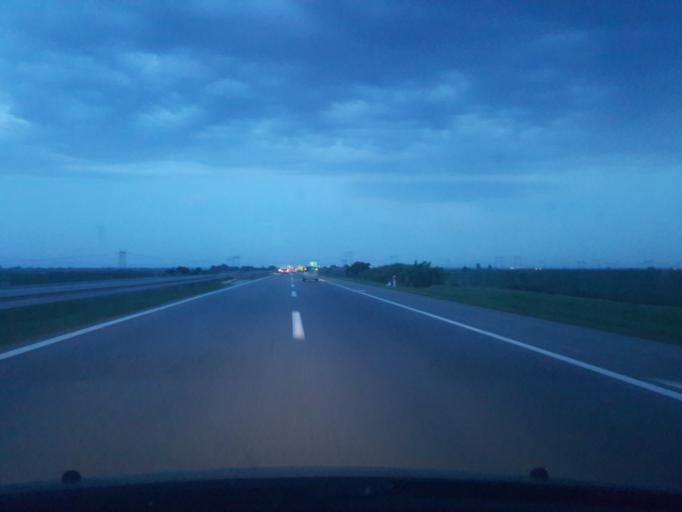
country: RS
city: Novi Karlovci
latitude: 45.0846
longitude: 20.1328
